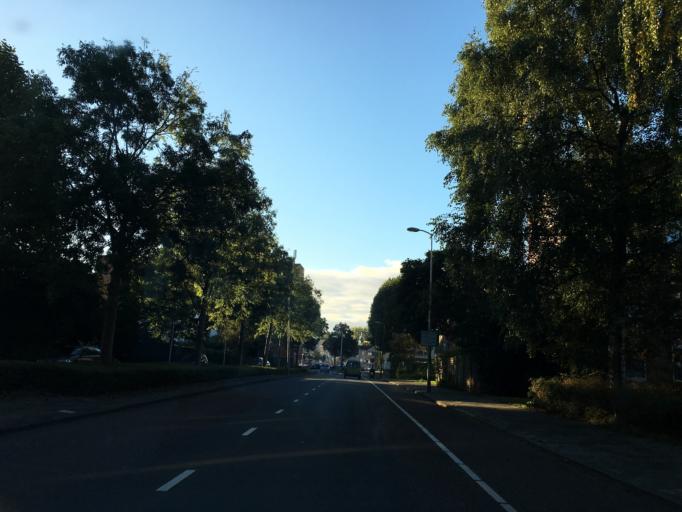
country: NL
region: South Holland
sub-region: Gemeente Capelle aan den IJssel
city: Capelle aan den IJssel
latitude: 51.9258
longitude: 4.5808
